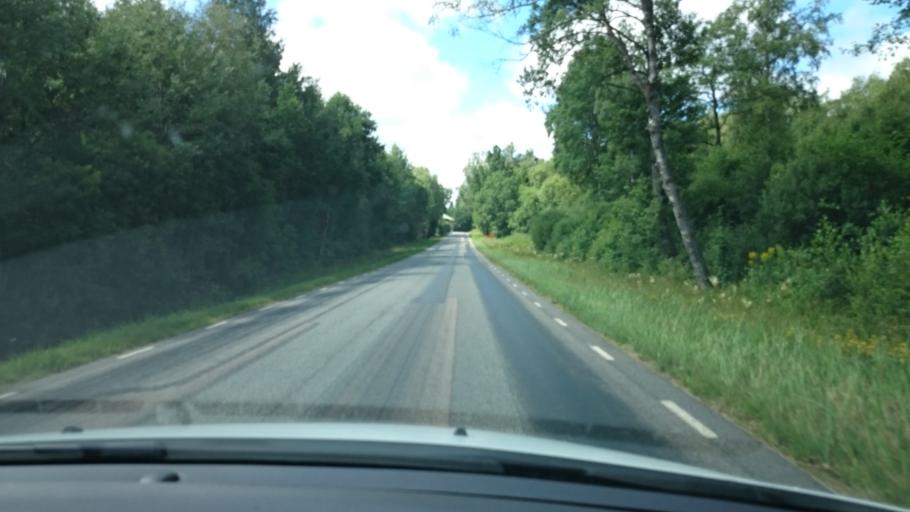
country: SE
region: Halland
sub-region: Hylte Kommun
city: Torup
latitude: 56.9579
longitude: 13.1007
